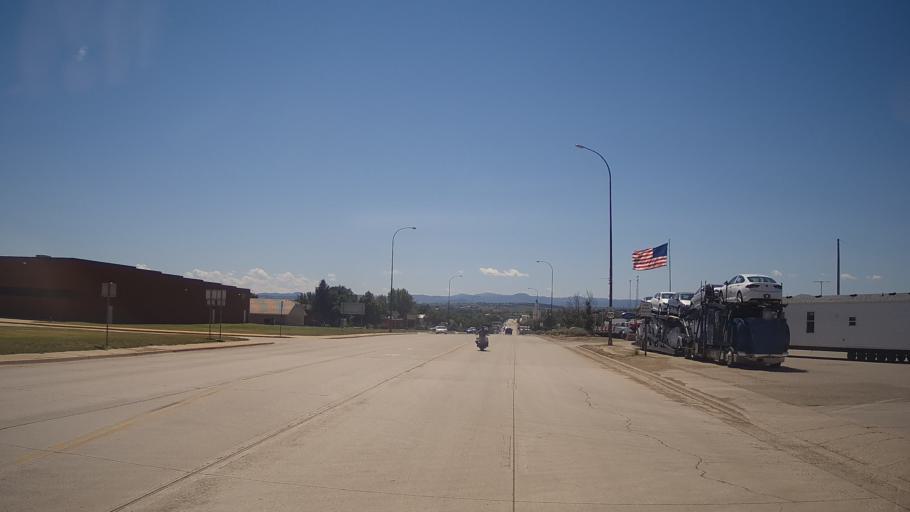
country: US
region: South Dakota
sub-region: Butte County
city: Belle Fourche
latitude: 44.6807
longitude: -103.8537
